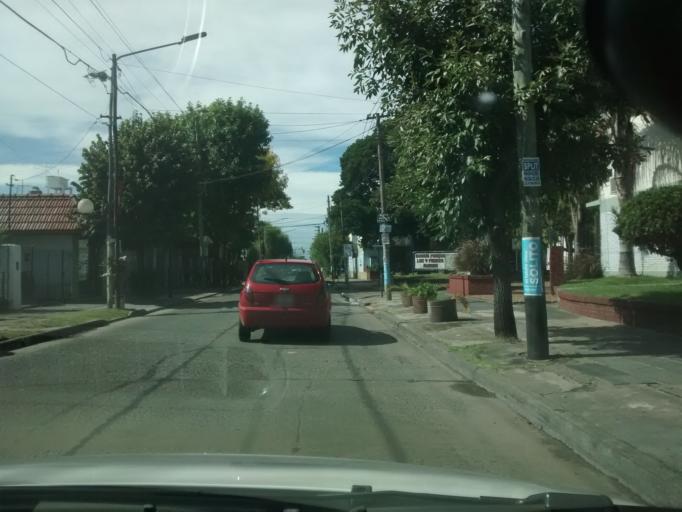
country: AR
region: Buenos Aires
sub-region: Partido de Moron
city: Moron
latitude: -34.6624
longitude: -58.6211
